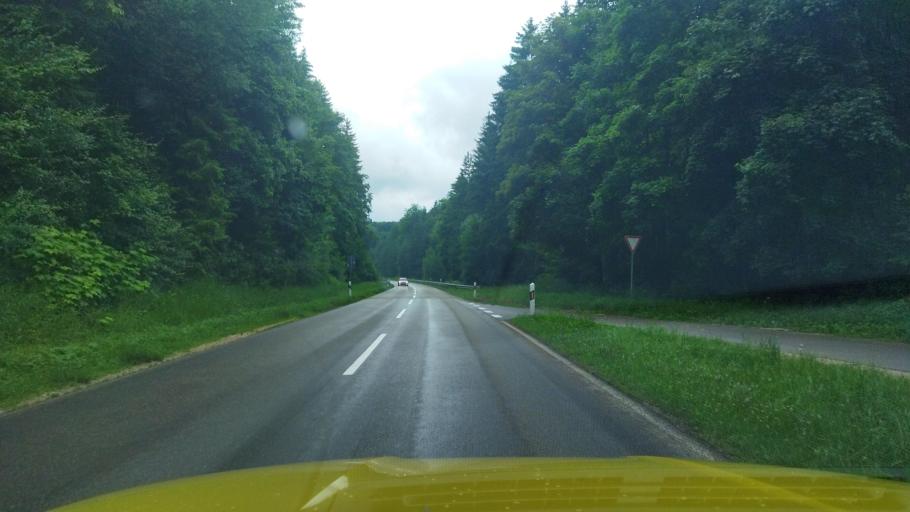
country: DE
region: Bavaria
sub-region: Lower Bavaria
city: Riedenburg
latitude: 48.9510
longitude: 11.6451
